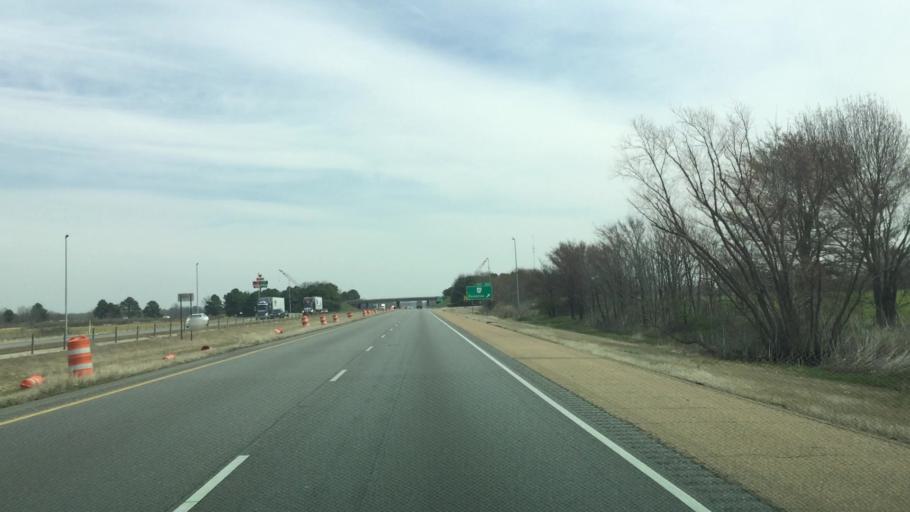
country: US
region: Arkansas
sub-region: Saint Francis County
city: Forrest City
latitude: 34.9811
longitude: -90.9107
